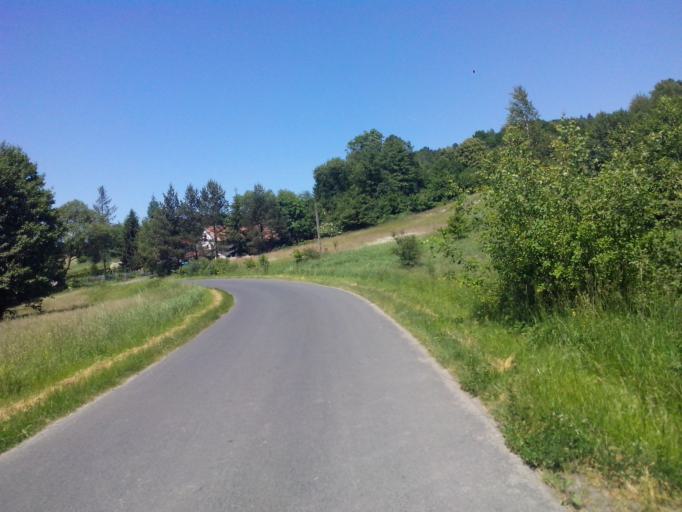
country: PL
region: Subcarpathian Voivodeship
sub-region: Powiat krosnienski
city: Wojaszowka
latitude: 49.8000
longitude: 21.7016
